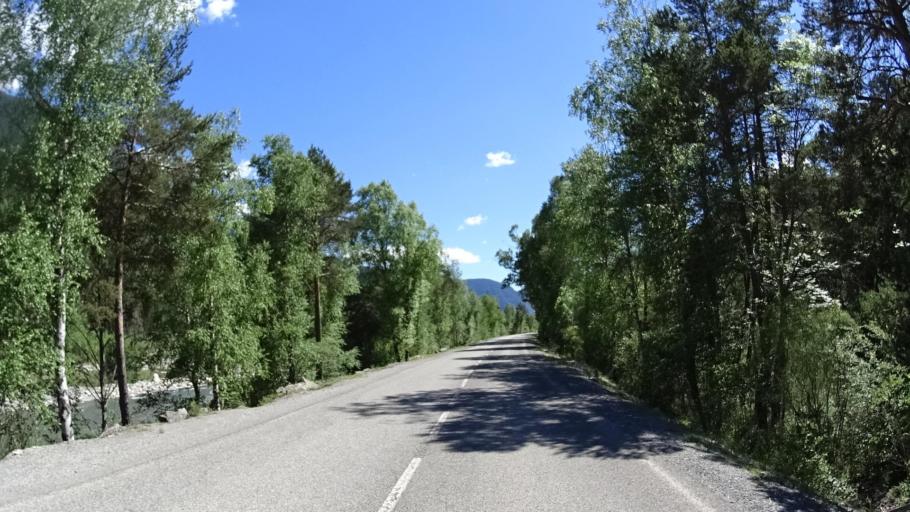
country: FR
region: Provence-Alpes-Cote d'Azur
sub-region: Departement des Alpes-de-Haute-Provence
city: Annot
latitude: 44.1494
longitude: 6.5979
